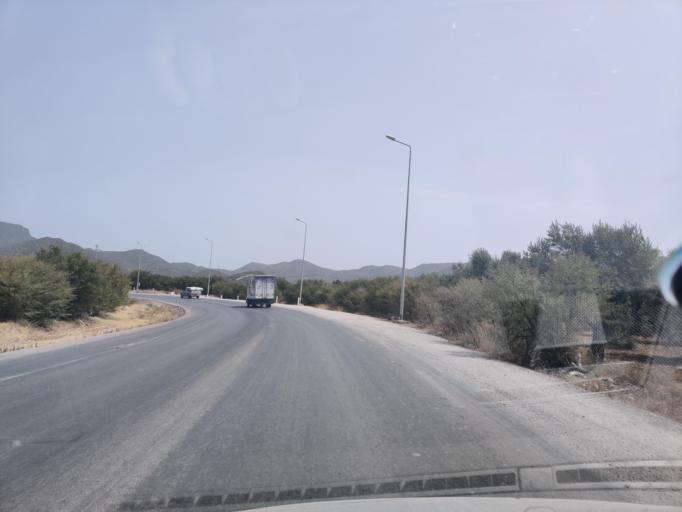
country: TN
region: Tunis
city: La Sebala du Mornag
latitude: 36.6652
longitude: 10.3247
